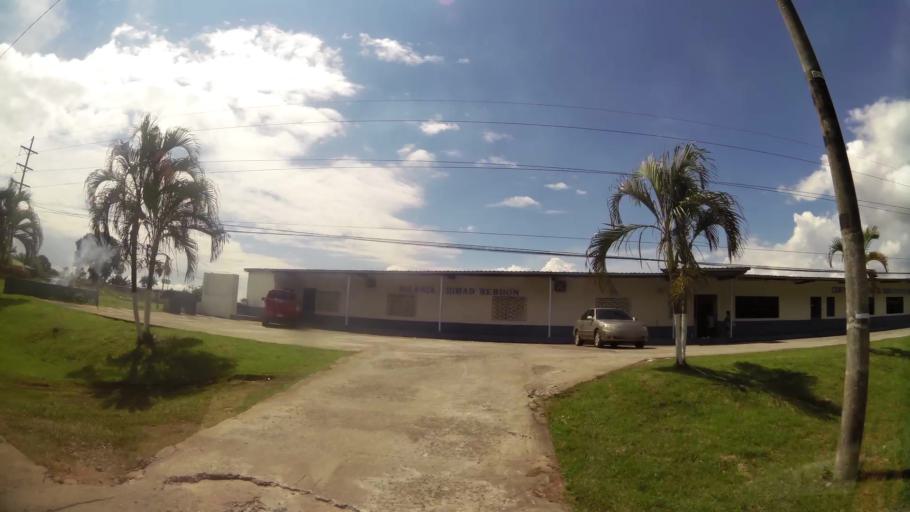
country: PA
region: Panama
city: San Vicente de Bique
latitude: 8.9196
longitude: -79.6954
